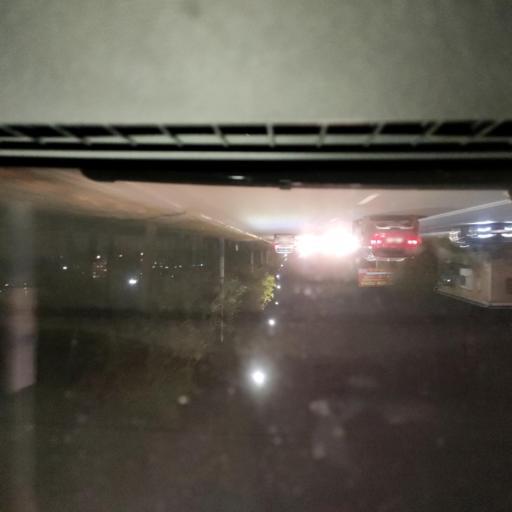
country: RU
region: Voronezj
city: Somovo
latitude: 51.7126
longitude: 39.2754
